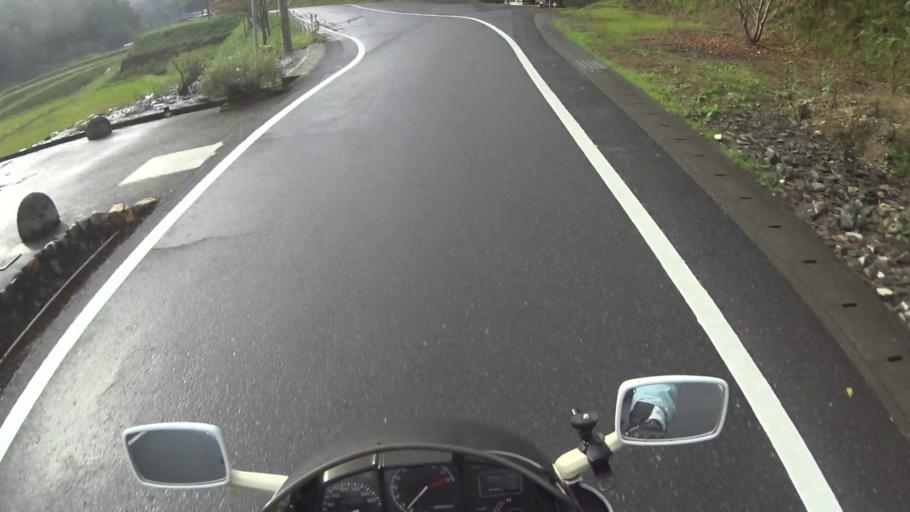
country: JP
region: Kyoto
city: Ayabe
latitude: 35.2862
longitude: 135.2381
